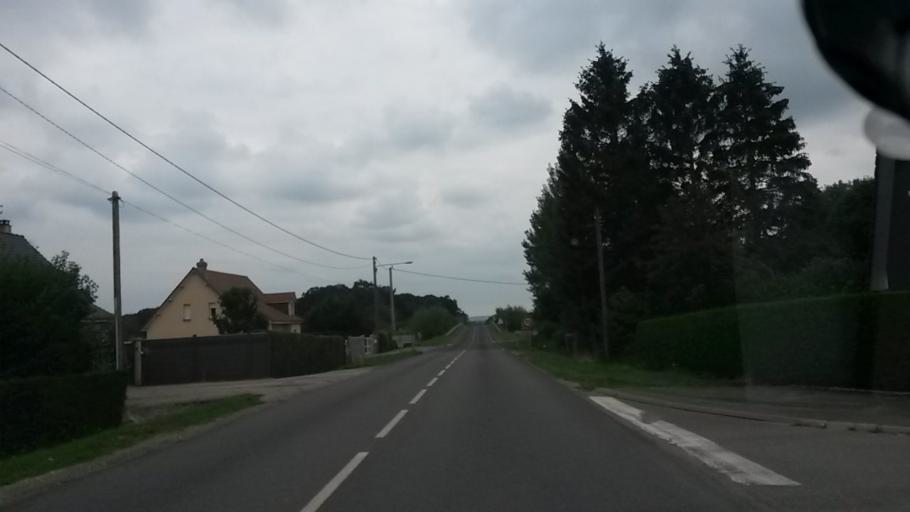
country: FR
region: Haute-Normandie
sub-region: Departement de la Seine-Maritime
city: Forges-les-Eaux
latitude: 49.6037
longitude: 1.5469
